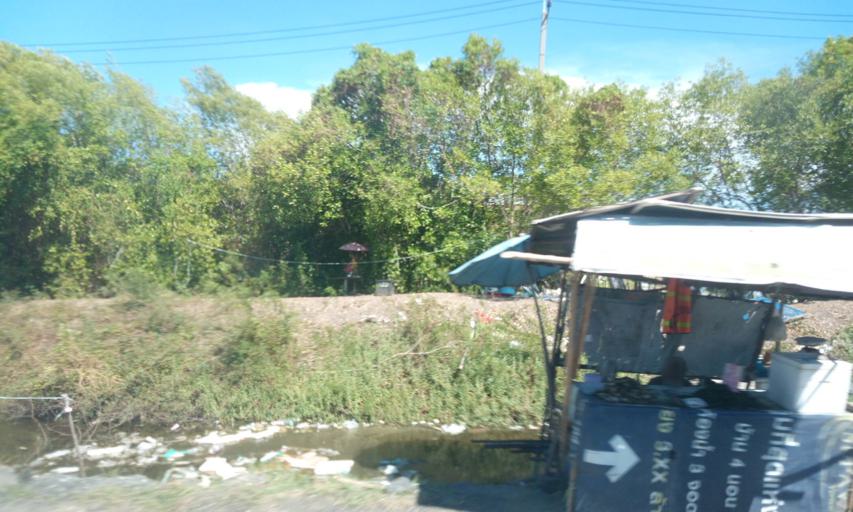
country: TH
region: Samut Prakan
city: Bang Bo District
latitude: 13.5081
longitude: 100.7815
